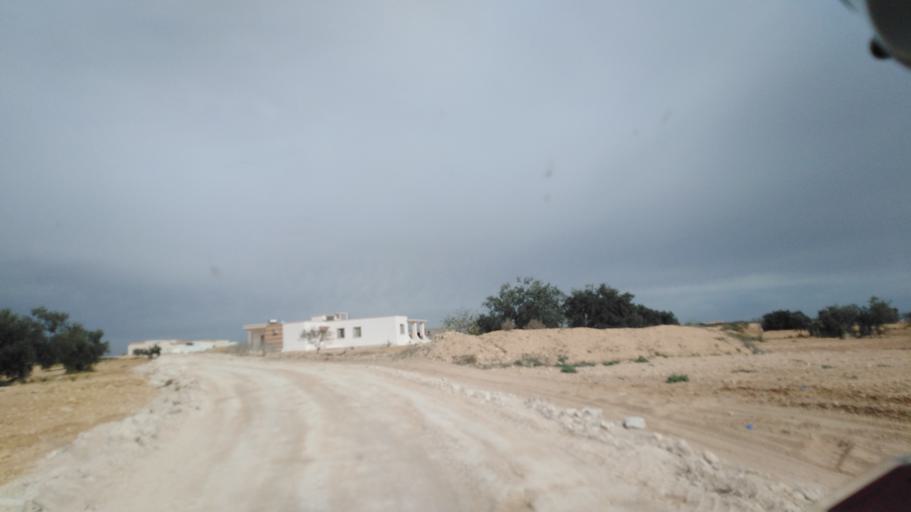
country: TN
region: Safaqis
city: Bi'r `Ali Bin Khalifah
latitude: 34.8133
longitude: 10.3076
